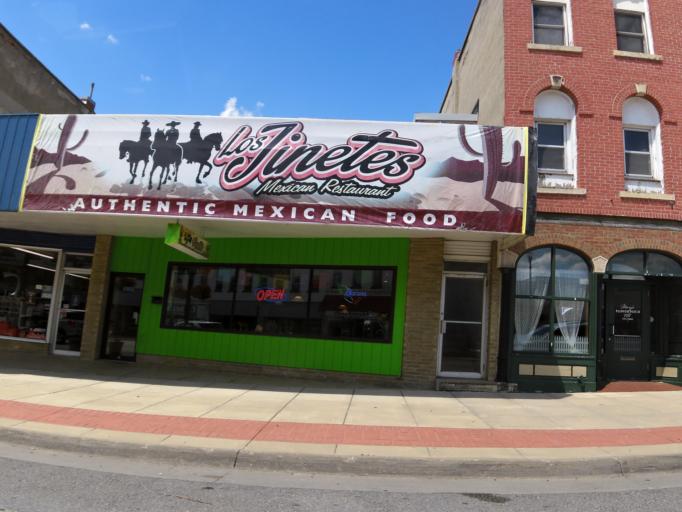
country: US
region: Iowa
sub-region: Buchanan County
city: Independence
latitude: 42.4688
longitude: -91.8922
